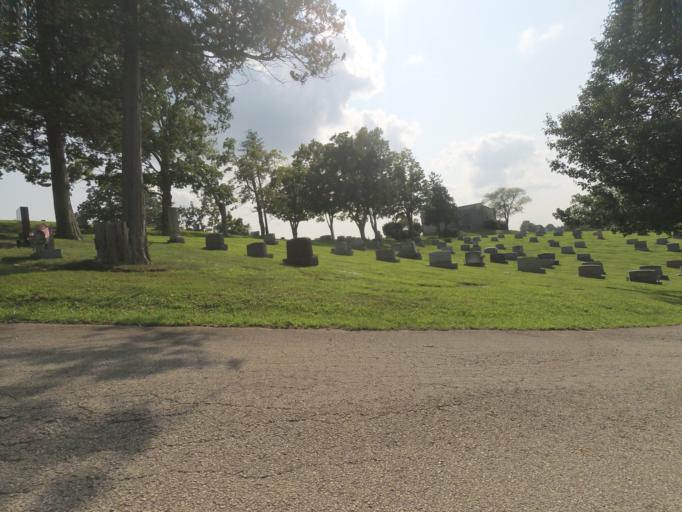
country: US
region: West Virginia
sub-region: Cabell County
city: Huntington
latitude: 38.4049
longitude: -82.3967
